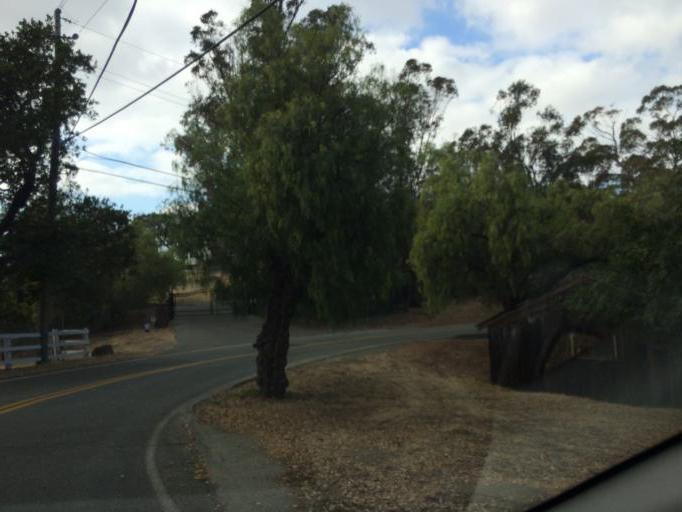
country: US
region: California
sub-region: Santa Clara County
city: East Foothills
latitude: 37.3896
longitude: -121.8061
